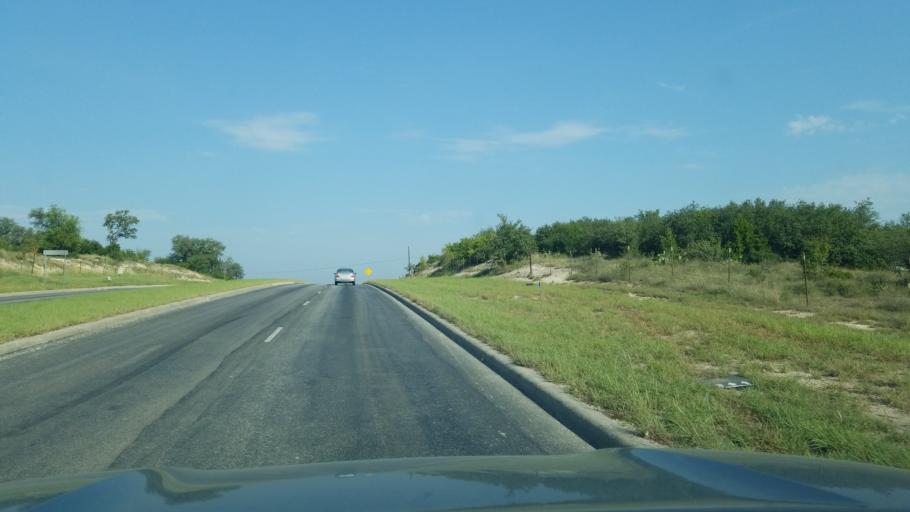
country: US
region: Texas
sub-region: Bexar County
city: Helotes
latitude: 29.4616
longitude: -98.7486
